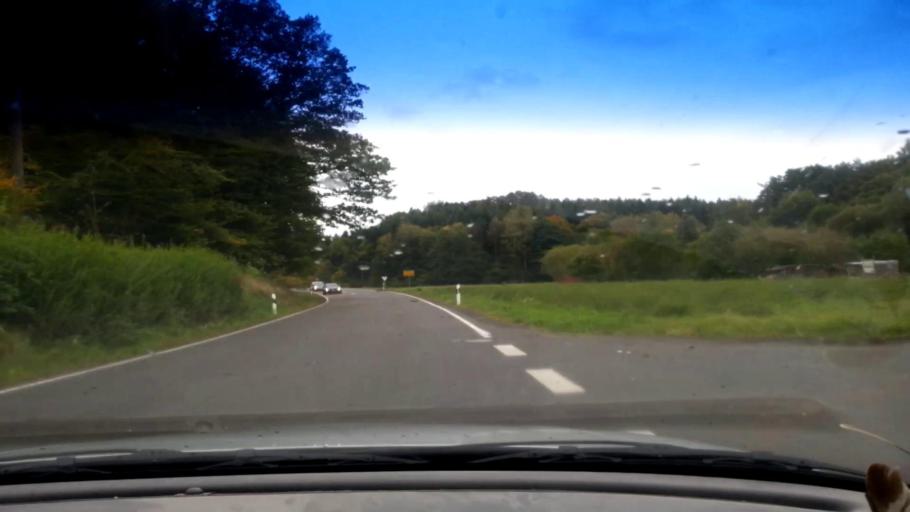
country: DE
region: Bavaria
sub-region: Regierungsbezirk Unterfranken
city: Stettfeld
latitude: 49.9981
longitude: 10.7484
